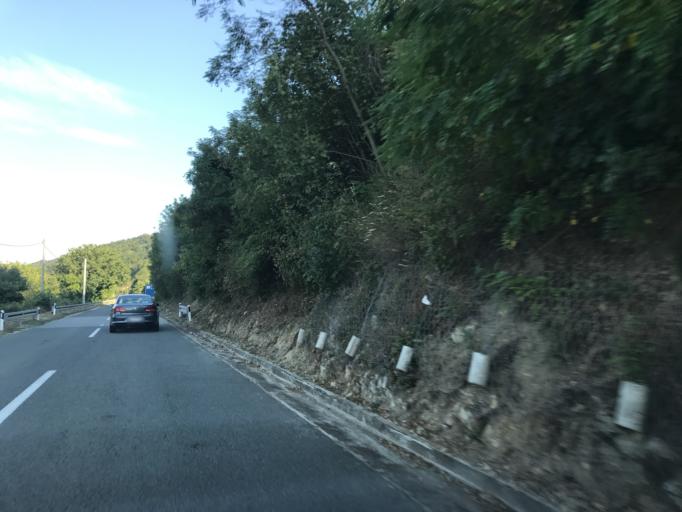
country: RO
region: Mehedinti
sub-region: Comuna Svinita
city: Svinita
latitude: 44.4792
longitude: 22.0949
